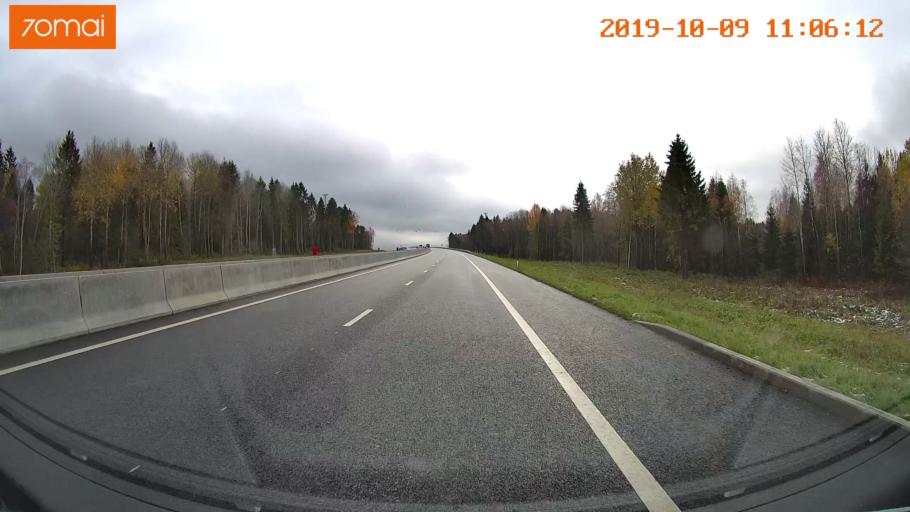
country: RU
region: Vologda
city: Vologda
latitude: 59.1895
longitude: 39.7590
